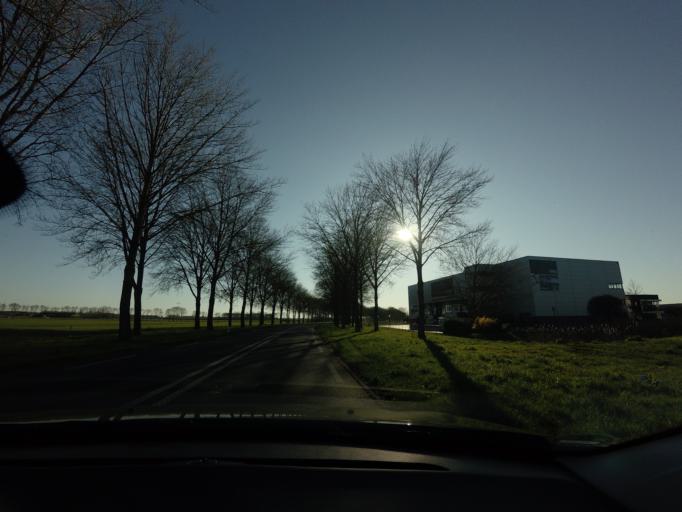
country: NL
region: Gelderland
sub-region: Gemeente Culemborg
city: Culemborg
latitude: 51.9408
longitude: 5.2277
